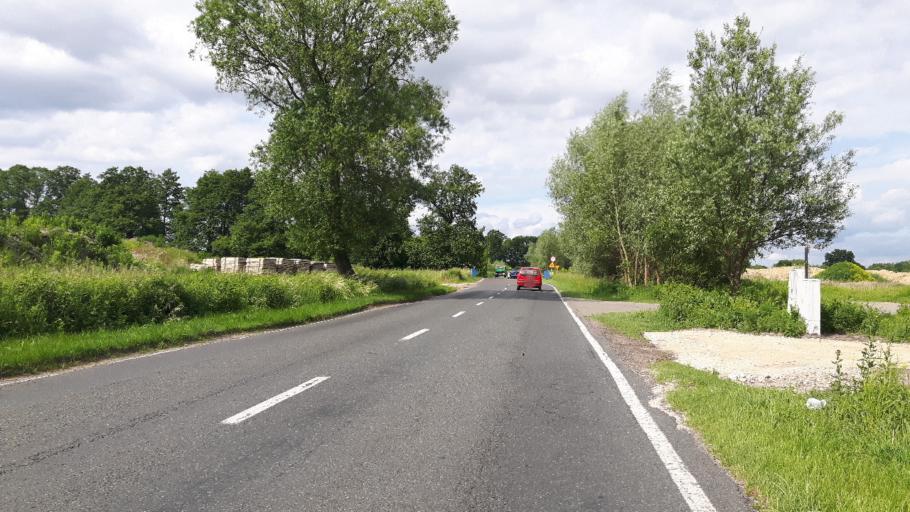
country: PL
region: West Pomeranian Voivodeship
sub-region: Szczecin
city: Szczecin
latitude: 53.4128
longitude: 14.7012
